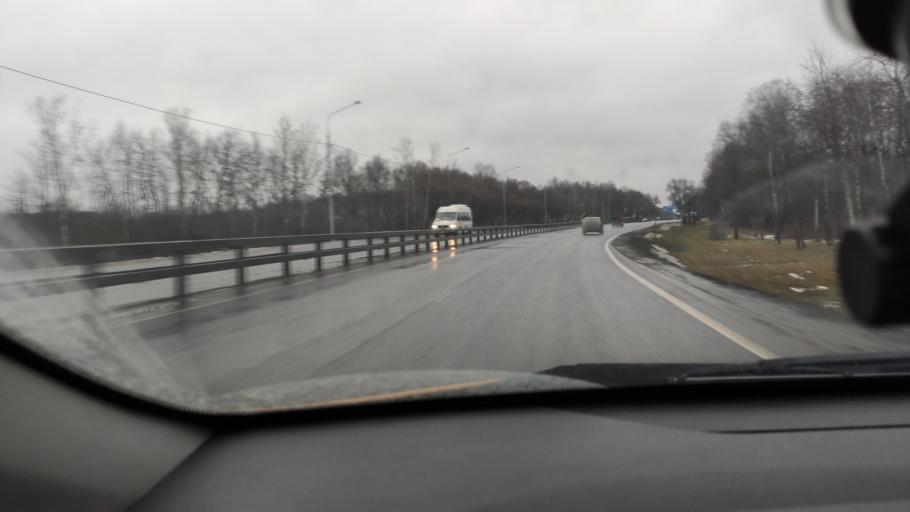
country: RU
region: Moskovskaya
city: Troitsk
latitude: 55.3092
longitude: 37.2272
